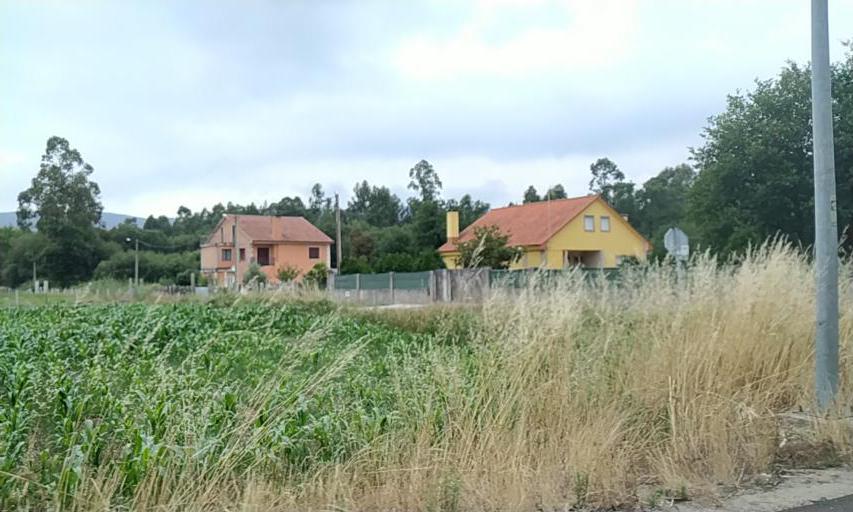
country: ES
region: Galicia
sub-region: Provincia de Pontevedra
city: Tomino
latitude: 41.9634
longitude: -8.7614
